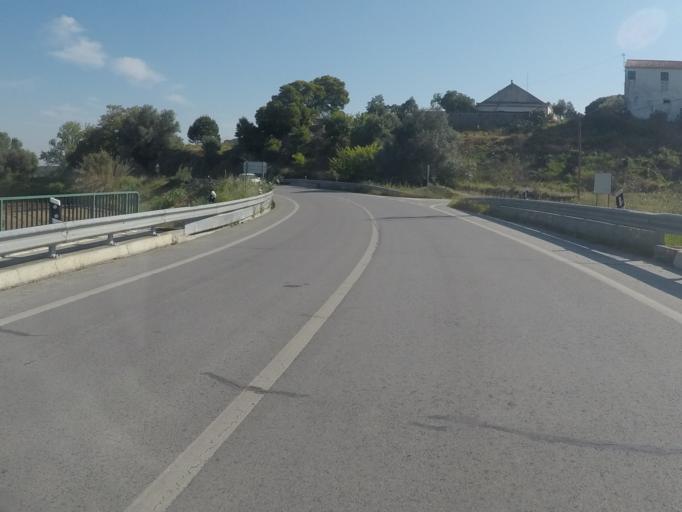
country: PT
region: Setubal
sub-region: Sesimbra
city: Sesimbra
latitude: 38.5021
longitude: -9.1488
